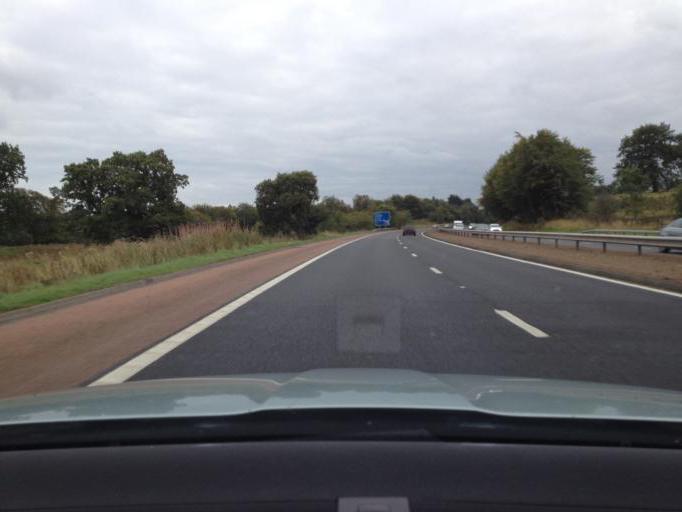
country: GB
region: Scotland
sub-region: Fife
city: Kelty
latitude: 56.1488
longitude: -3.3930
